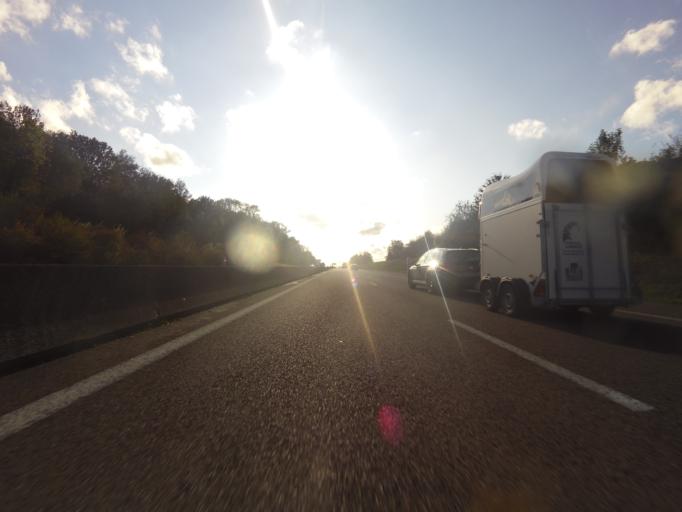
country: FR
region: Picardie
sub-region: Departement de la Somme
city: Saleux
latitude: 49.8700
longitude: 2.1911
